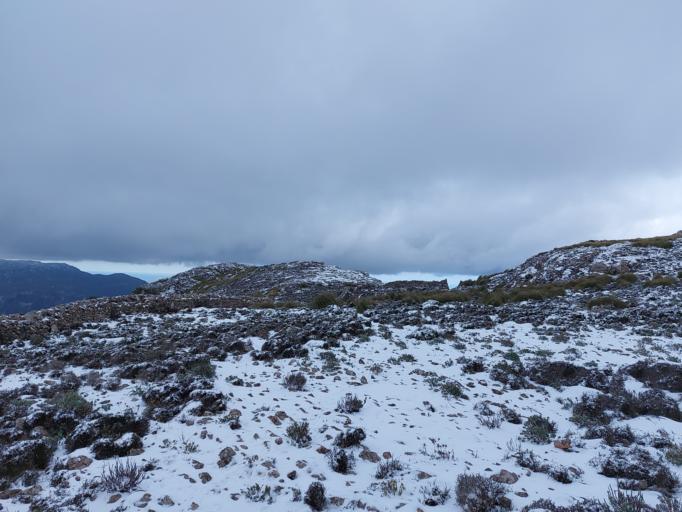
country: ES
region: Balearic Islands
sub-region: Illes Balears
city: Fornalutx
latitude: 39.7739
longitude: 2.7609
